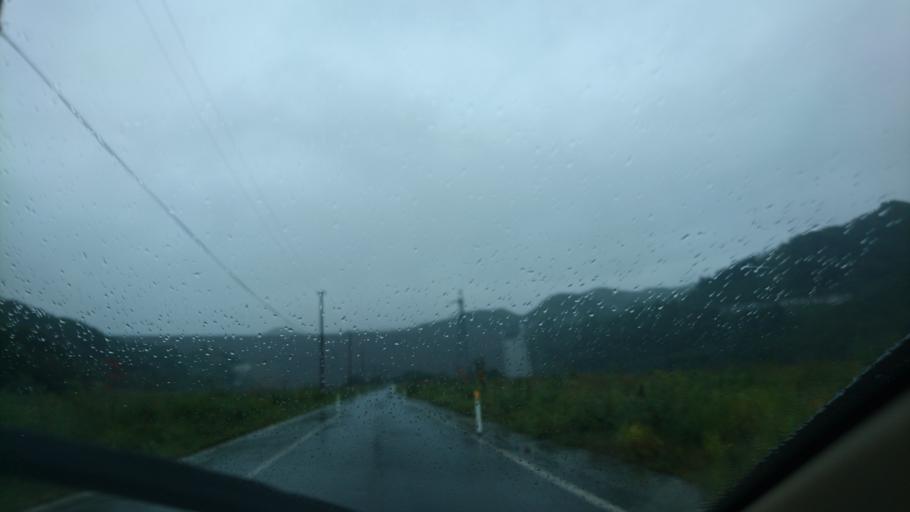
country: JP
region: Iwate
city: Mizusawa
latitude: 39.1200
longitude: 140.9307
